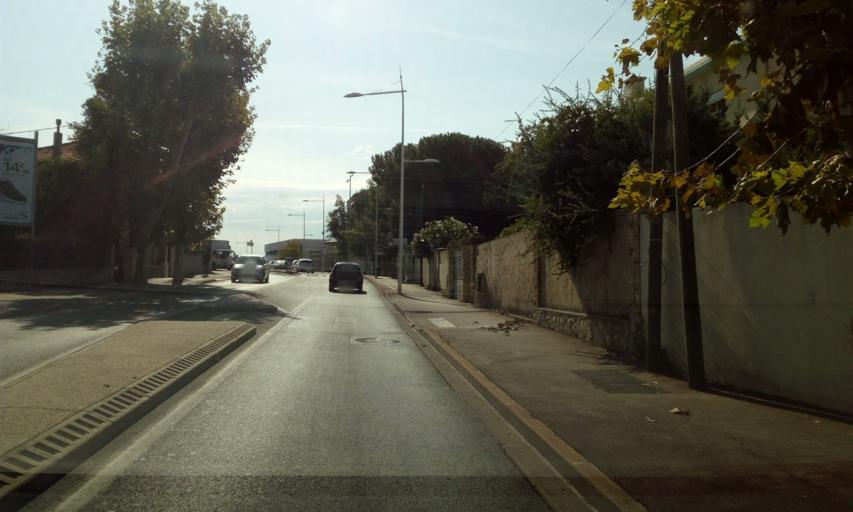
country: FR
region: Provence-Alpes-Cote d'Azur
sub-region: Departement du Var
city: La Valette-du-Var
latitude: 43.1200
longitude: 5.9769
